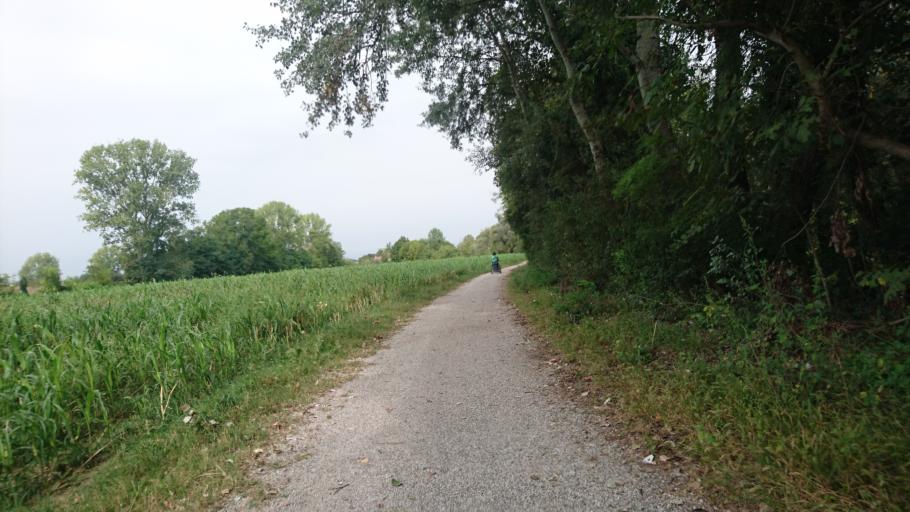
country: IT
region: Veneto
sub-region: Provincia di Padova
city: Grantorto
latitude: 45.5742
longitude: 11.7586
